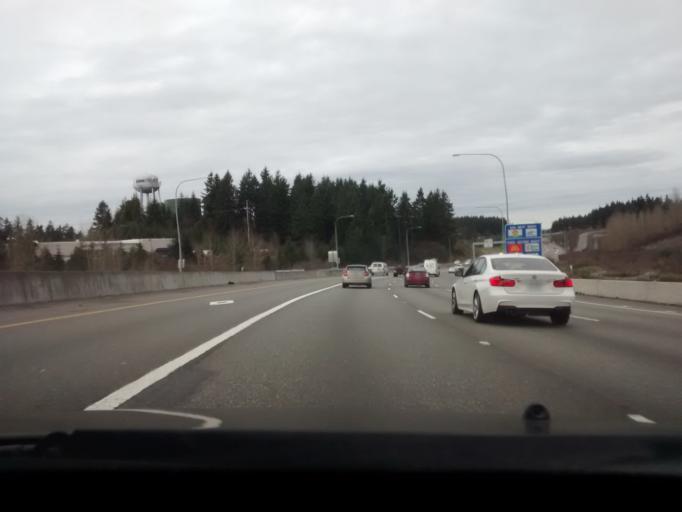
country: US
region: Washington
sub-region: Pierce County
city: Fircrest
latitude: 47.2357
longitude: -122.4984
